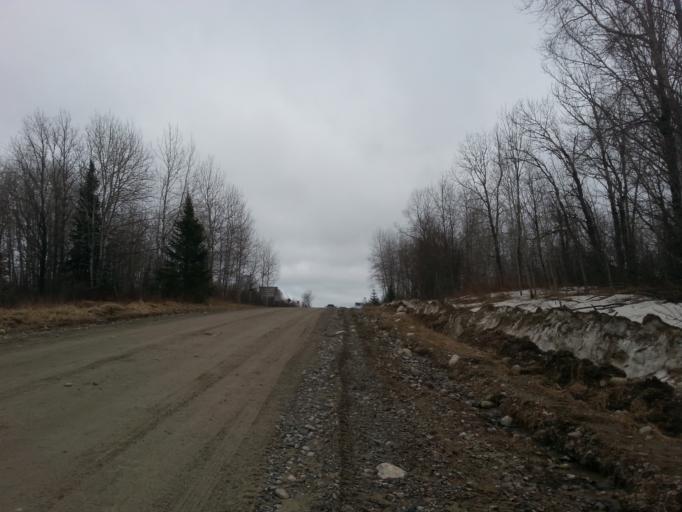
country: CA
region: Quebec
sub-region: Abitibi-Temiscamingue
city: La Sarre
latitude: 48.9520
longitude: -79.5199
